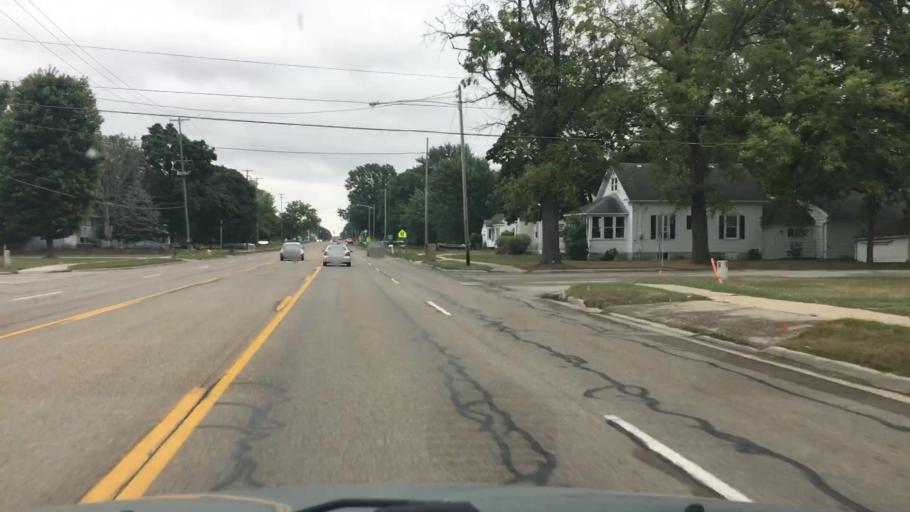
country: US
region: Michigan
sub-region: Ottawa County
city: Hudsonville
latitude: 42.9071
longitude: -85.8381
